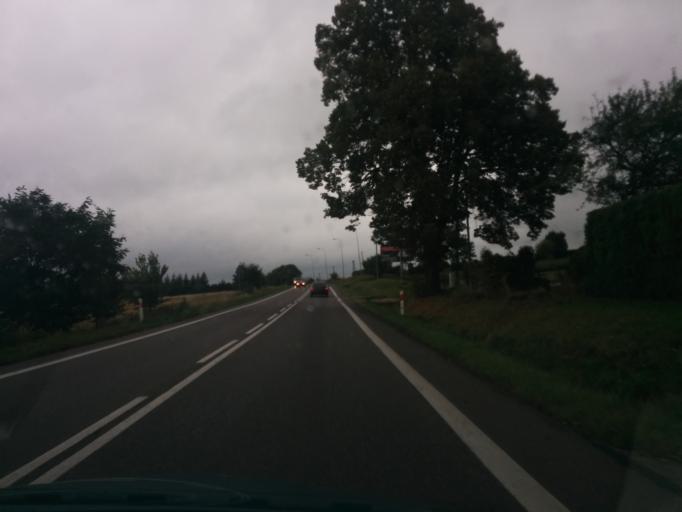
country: PL
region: Subcarpathian Voivodeship
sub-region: Powiat sanocki
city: Strachocina
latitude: 49.5891
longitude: 22.1360
